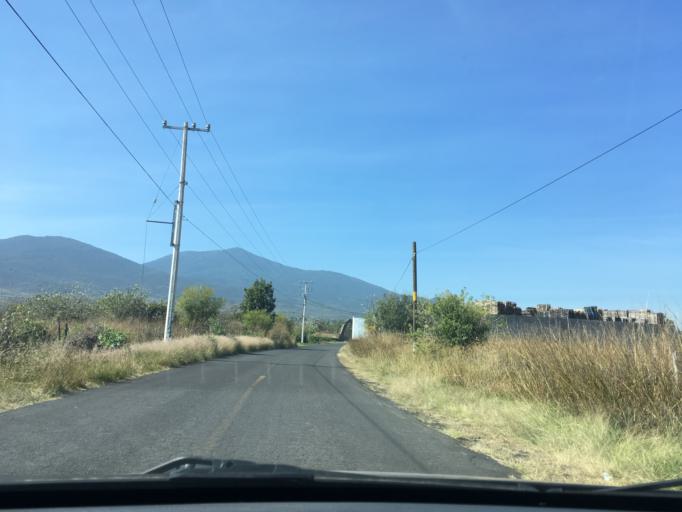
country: MX
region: Michoacan
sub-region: Morelia
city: La Mintzita (Piedra Dura)
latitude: 19.6482
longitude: -101.3015
